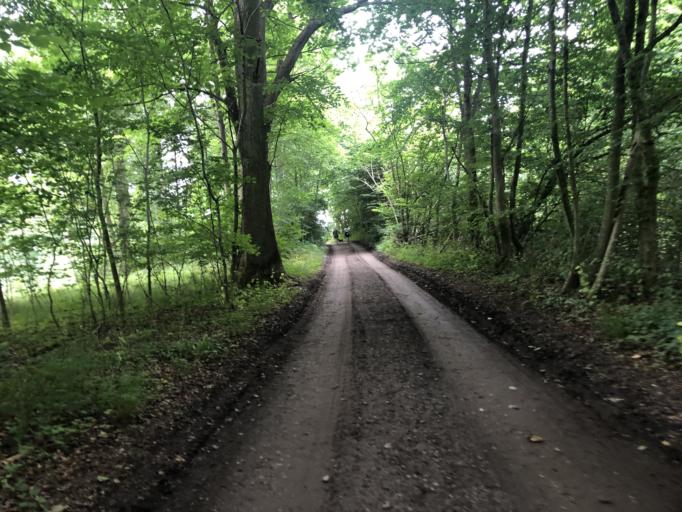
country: DK
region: South Denmark
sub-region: Vejle Kommune
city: Borkop
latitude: 55.6078
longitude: 9.6792
